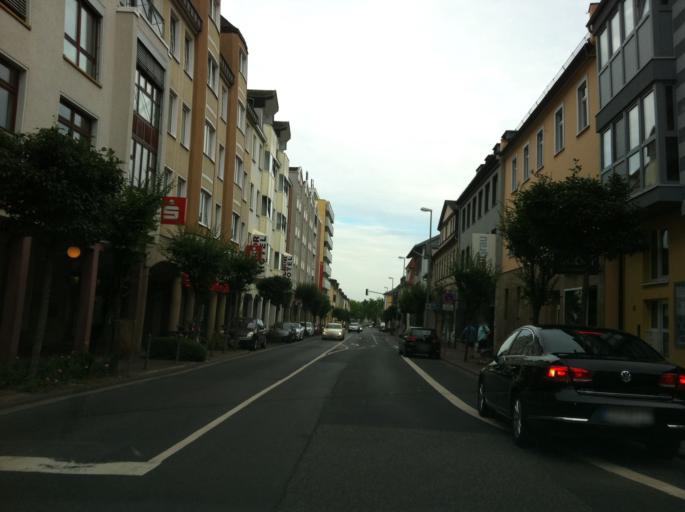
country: DE
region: Hesse
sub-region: Regierungsbezirk Darmstadt
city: Bad Soden am Taunus
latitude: 50.1453
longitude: 8.5003
